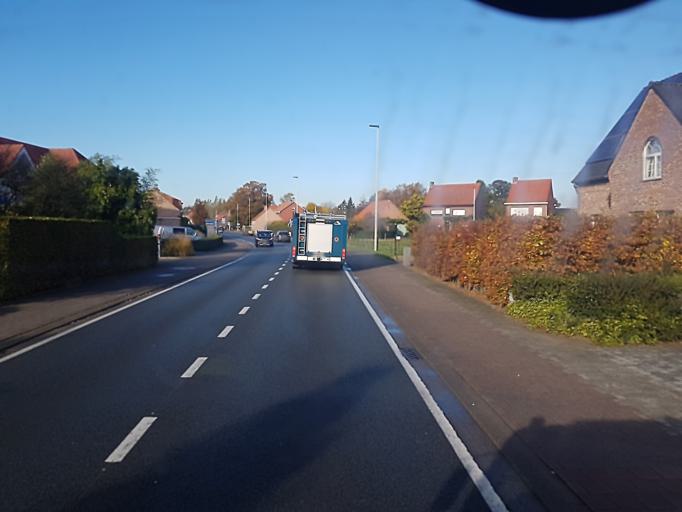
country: BE
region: Flanders
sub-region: Provincie Antwerpen
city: Brecht
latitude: 51.3458
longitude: 4.6489
